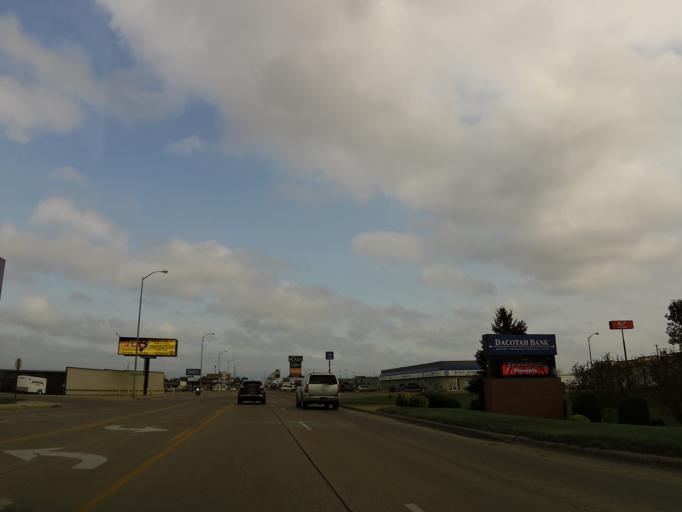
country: US
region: South Dakota
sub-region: Codington County
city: Watertown
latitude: 44.8897
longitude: -97.0937
